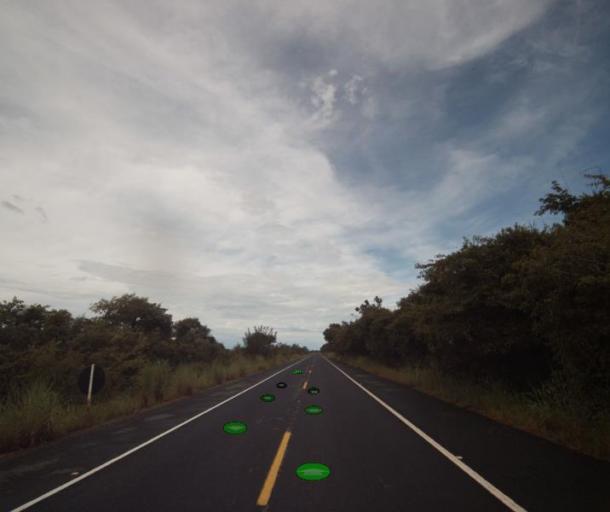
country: BR
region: Goias
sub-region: Sao Miguel Do Araguaia
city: Sao Miguel do Araguaia
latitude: -13.2356
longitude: -50.5569
